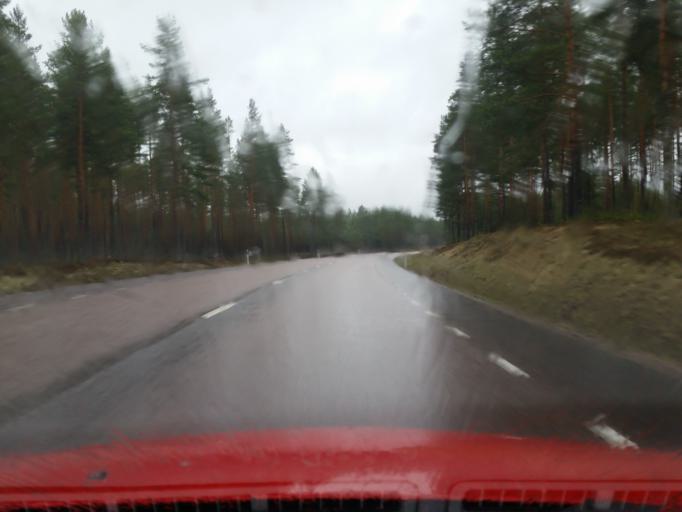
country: SE
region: Dalarna
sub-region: Leksand Municipality
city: Smedby
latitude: 60.6562
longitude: 15.0784
